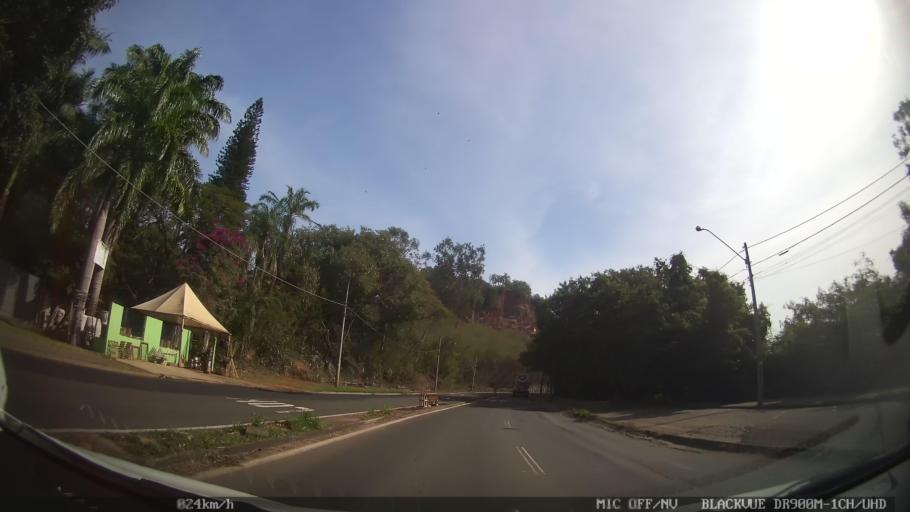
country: BR
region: Sao Paulo
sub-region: Piracicaba
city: Piracicaba
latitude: -22.7183
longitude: -47.6769
